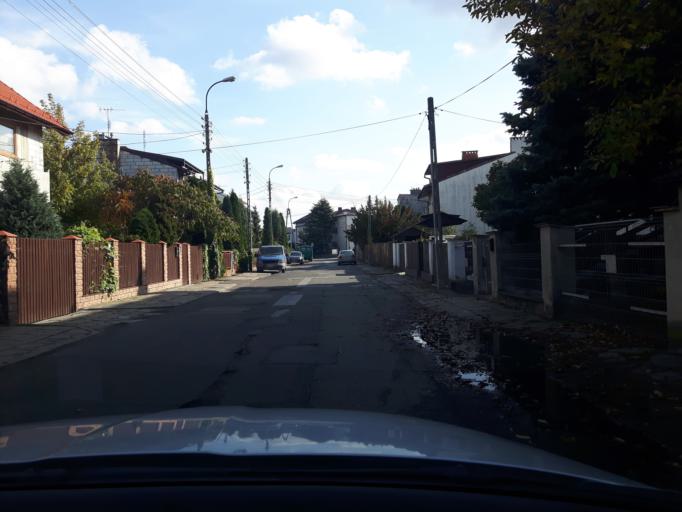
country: PL
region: Masovian Voivodeship
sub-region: Warszawa
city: Targowek
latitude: 52.2794
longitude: 21.0712
